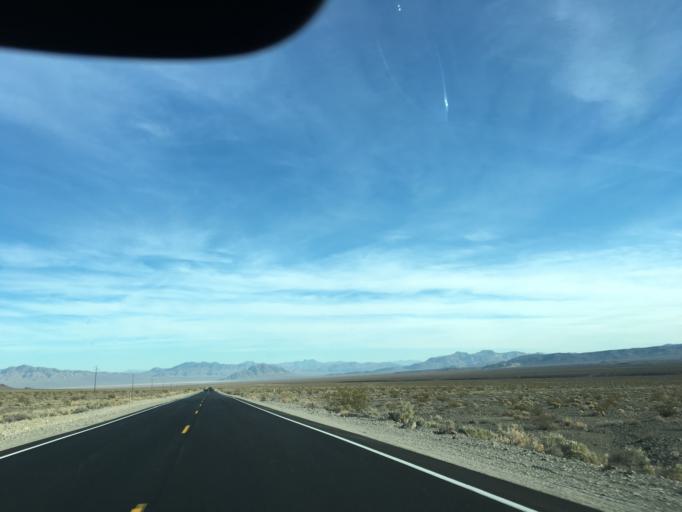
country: US
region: Nevada
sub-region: Nye County
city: Pahrump
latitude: 36.3257
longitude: -116.5646
